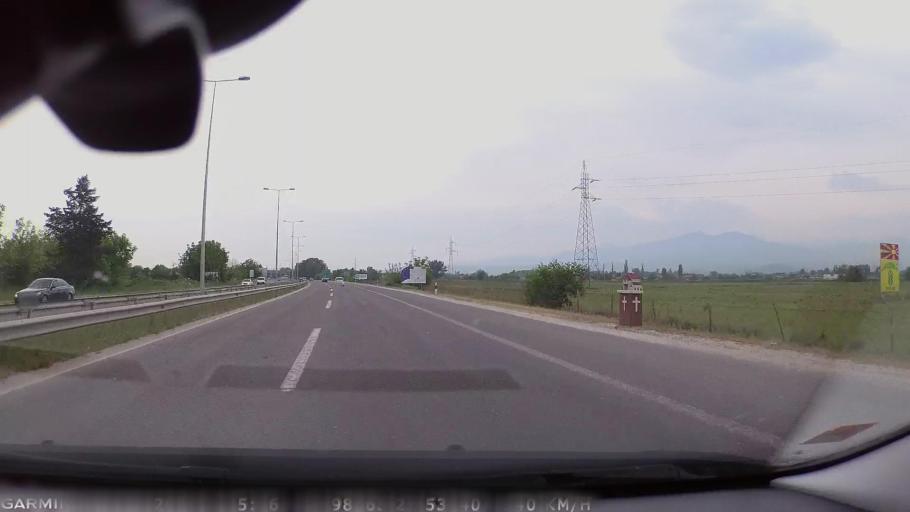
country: MK
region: Ilinden
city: Jurumleri
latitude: 41.9841
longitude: 21.5384
